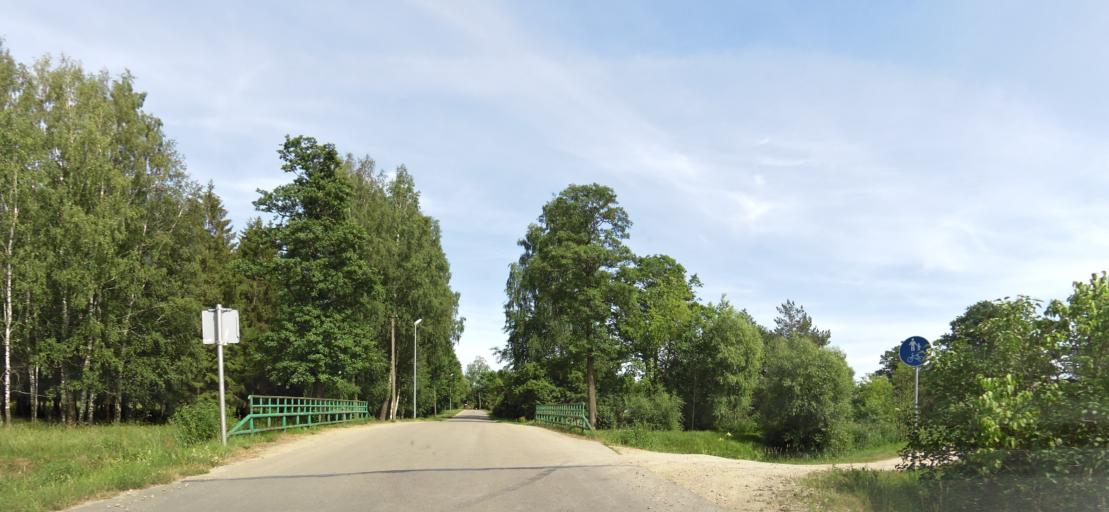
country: LT
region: Panevezys
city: Pasvalys
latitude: 55.9316
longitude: 24.3424
